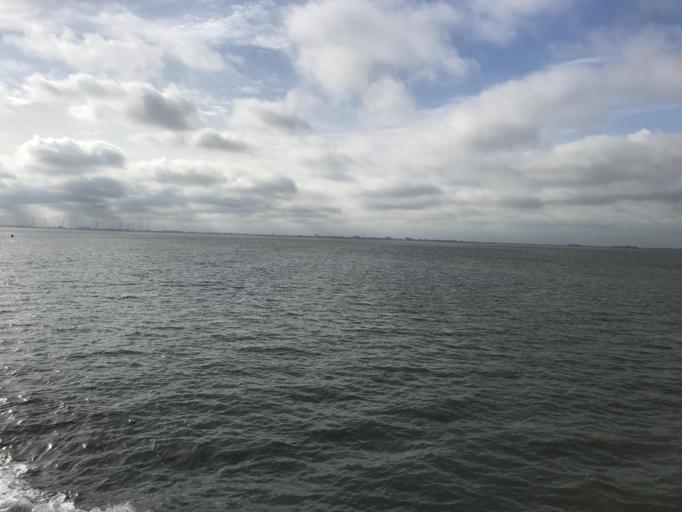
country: NL
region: Groningen
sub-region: Gemeente Delfzijl
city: Delfzijl
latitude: 53.3896
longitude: 6.9589
